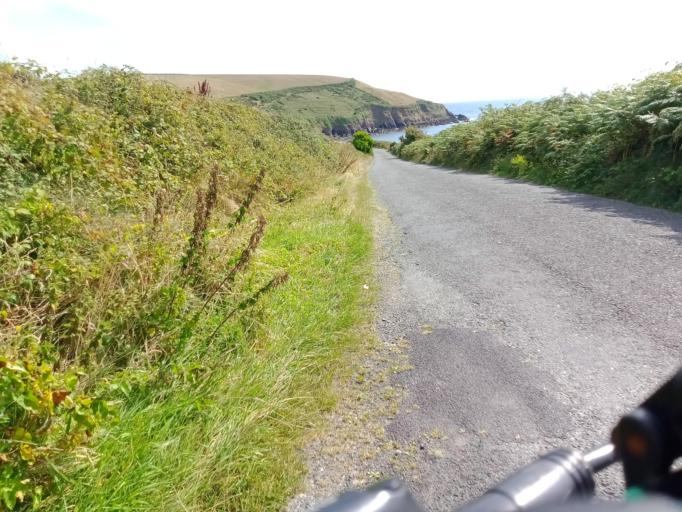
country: IE
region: Munster
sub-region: Waterford
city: Dungarvan
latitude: 52.1061
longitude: -7.5149
